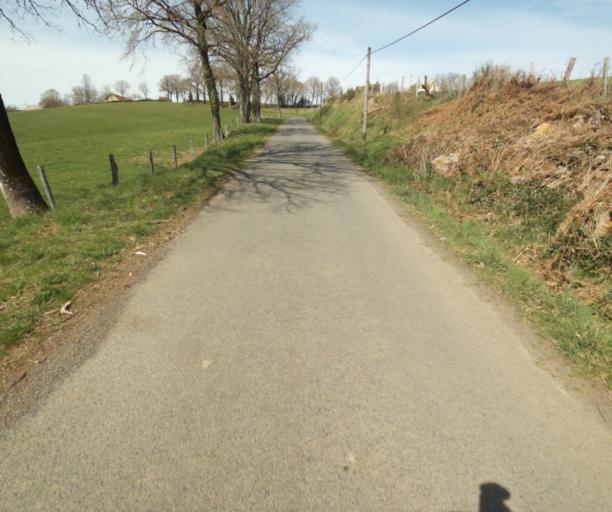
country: FR
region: Limousin
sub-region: Departement de la Correze
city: Naves
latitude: 45.3664
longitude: 1.7784
